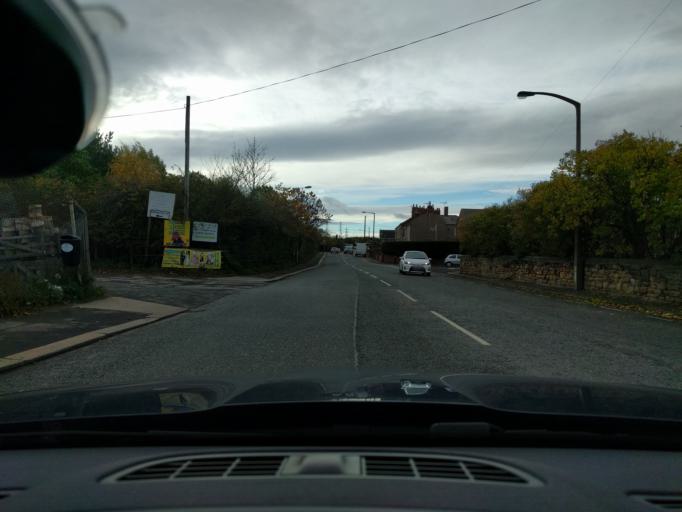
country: GB
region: England
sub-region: Northumberland
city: Bedlington
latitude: 55.1267
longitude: -1.5615
